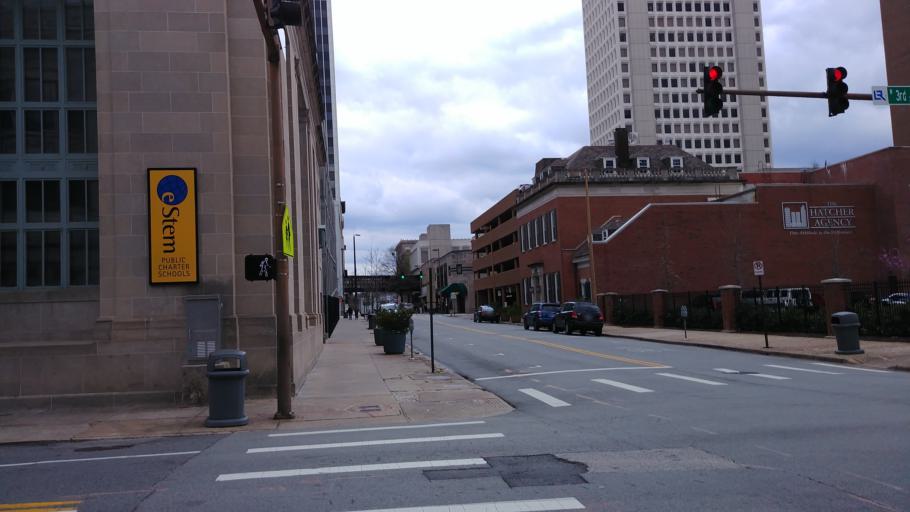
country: US
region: Arkansas
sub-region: Pulaski County
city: Little Rock
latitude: 34.7464
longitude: -92.2719
